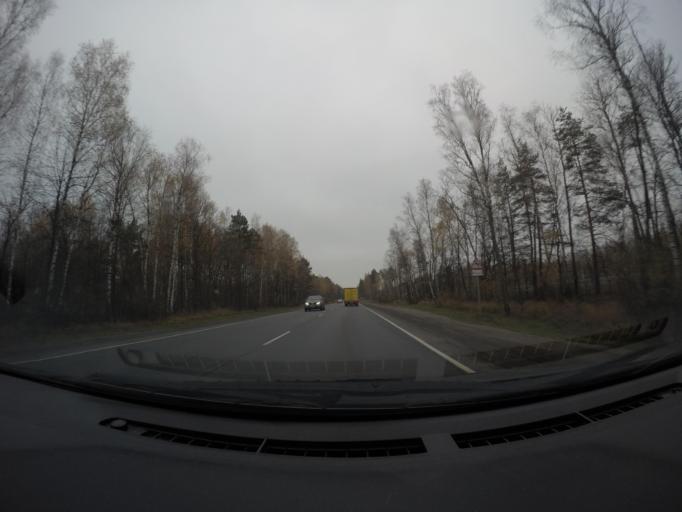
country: RU
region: Moskovskaya
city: Gzhel'
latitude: 55.5689
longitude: 38.3923
